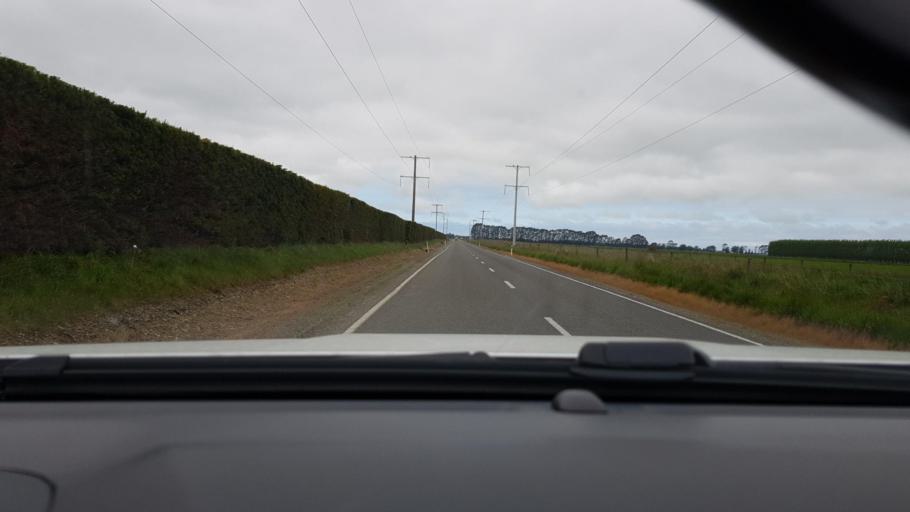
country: NZ
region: Otago
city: Oamaru
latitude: -44.9647
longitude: 171.0407
